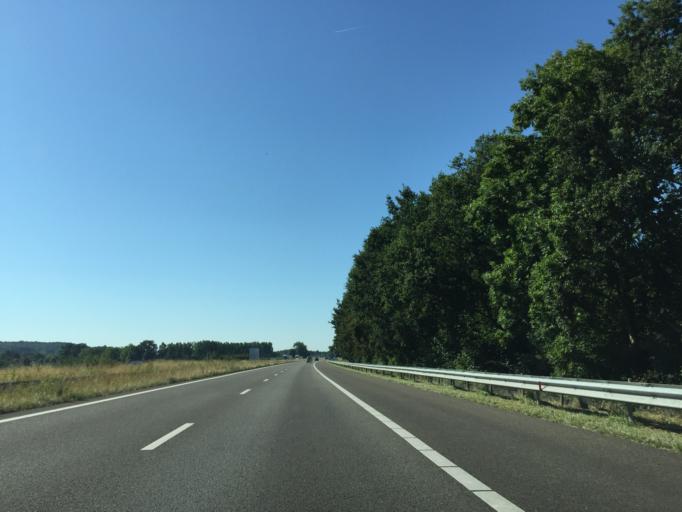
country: NL
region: Limburg
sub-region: Eijsden-Margraten
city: Eijsden
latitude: 50.8068
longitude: 5.7240
